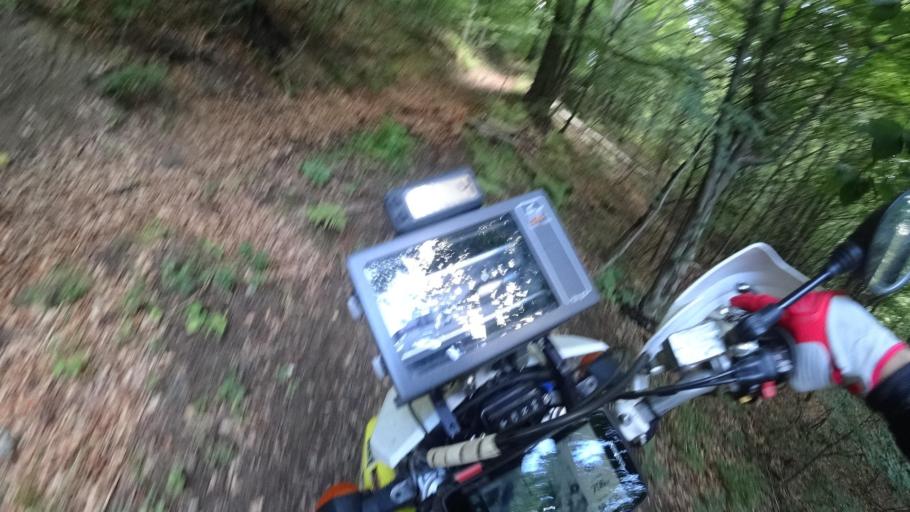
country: HR
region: Karlovacka
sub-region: Grad Ogulin
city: Ogulin
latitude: 45.2328
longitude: 15.1814
